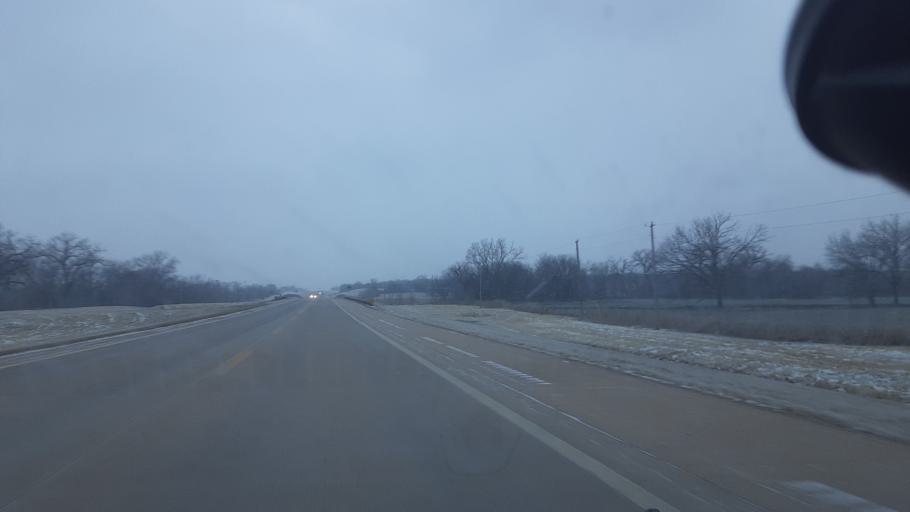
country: US
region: Oklahoma
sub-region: Payne County
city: Perkins
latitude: 35.9859
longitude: -97.1165
